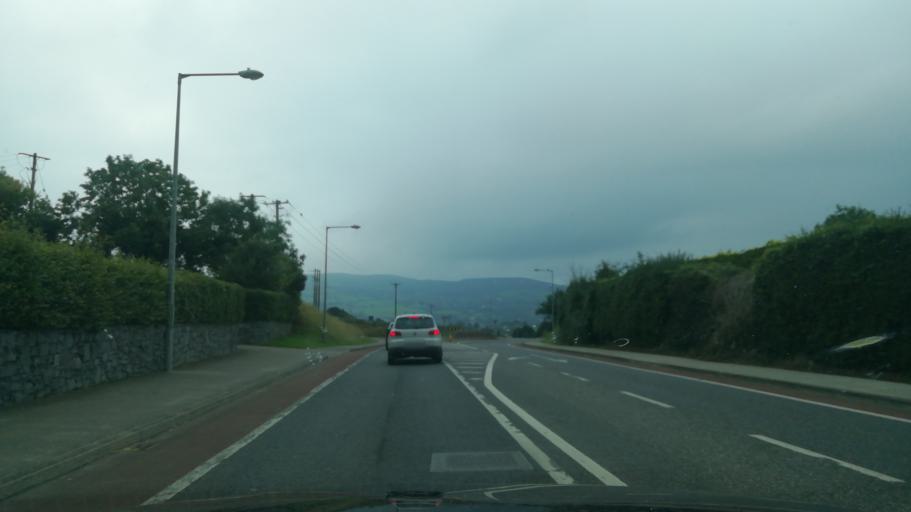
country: IE
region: Munster
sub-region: South Tipperary
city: Cluain Meala
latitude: 52.3700
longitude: -7.6997
